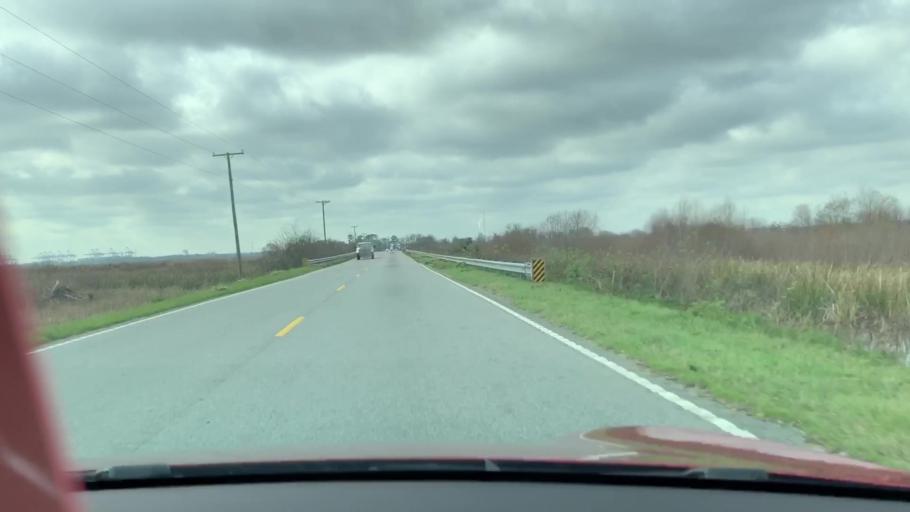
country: US
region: Georgia
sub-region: Chatham County
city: Port Wentworth
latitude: 32.1702
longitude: -81.1048
